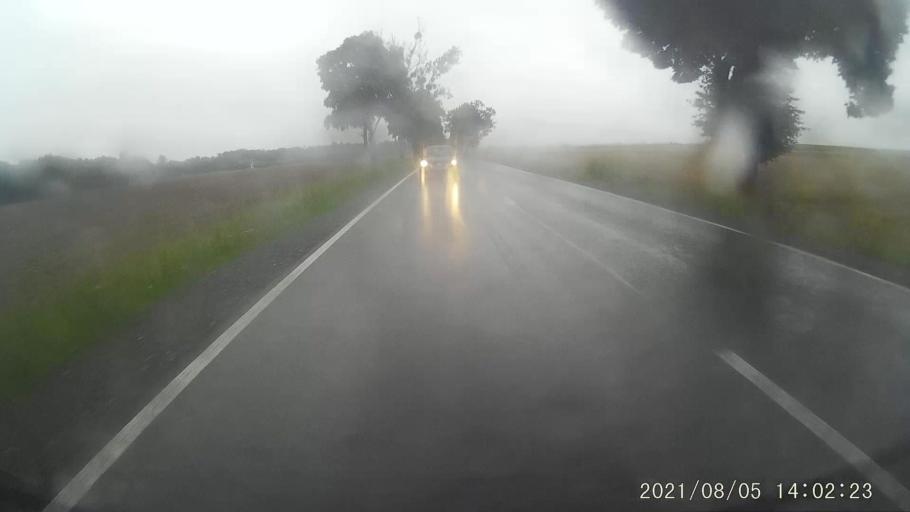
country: PL
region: Opole Voivodeship
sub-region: Powiat krapkowicki
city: Strzeleczki
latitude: 50.4551
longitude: 17.8760
